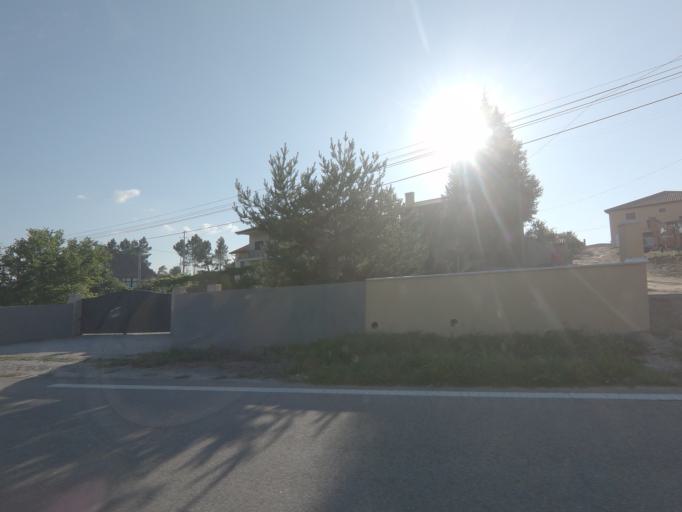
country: PT
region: Vila Real
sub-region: Chaves
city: Chaves
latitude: 41.7956
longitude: -7.4232
